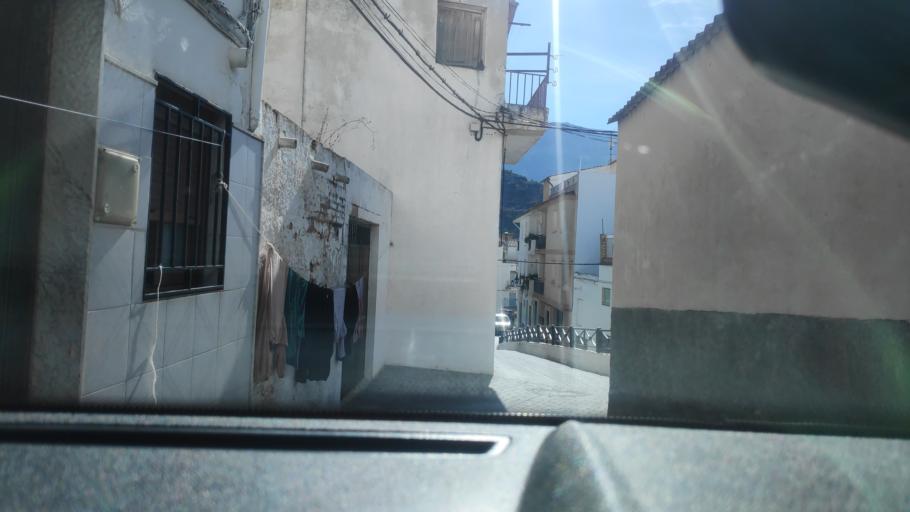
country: ES
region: Andalusia
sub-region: Provincia de Jaen
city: Torres
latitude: 37.7867
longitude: -3.5088
